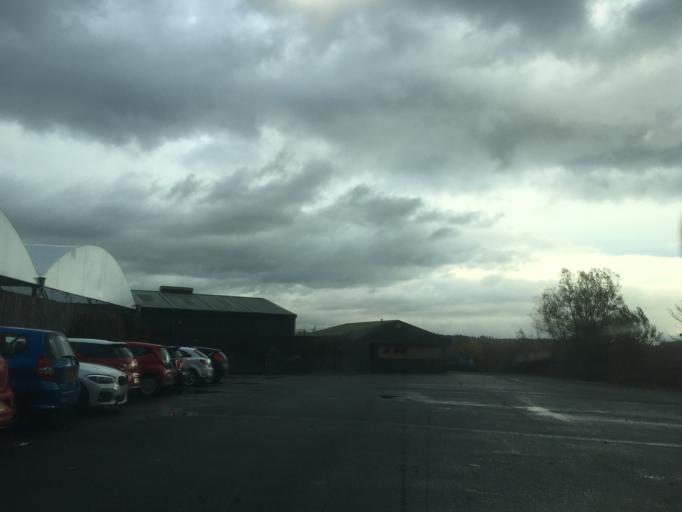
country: GB
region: Scotland
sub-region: Stirling
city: Bridge of Allan
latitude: 56.1397
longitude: -3.9793
